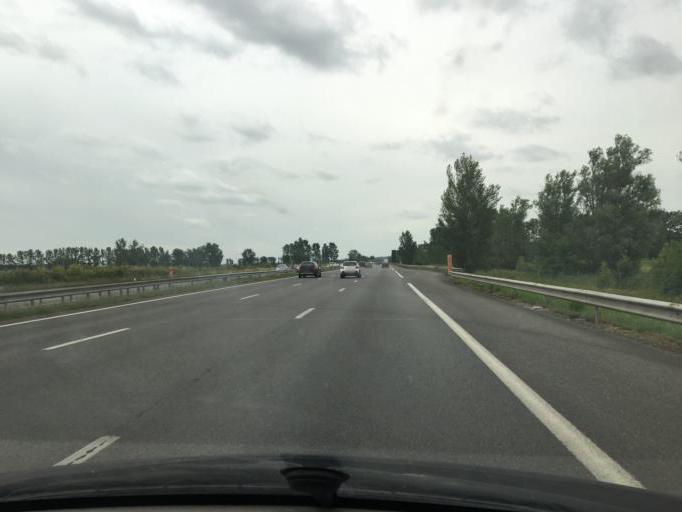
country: FR
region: Midi-Pyrenees
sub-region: Departement de la Haute-Garonne
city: Labege
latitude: 43.5132
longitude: 1.5274
